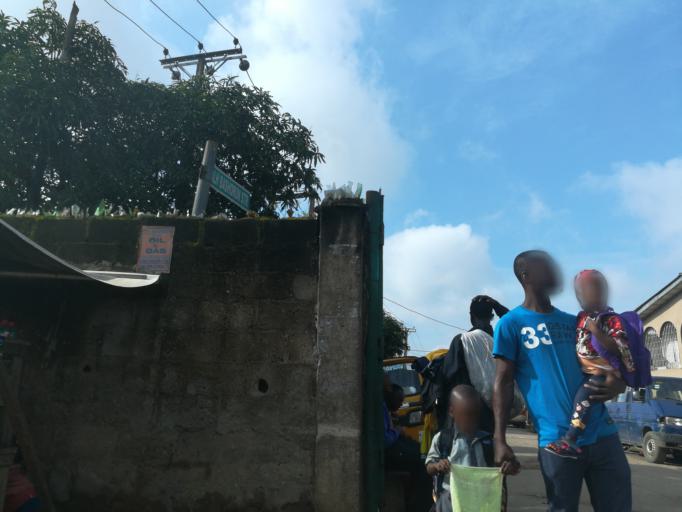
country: NG
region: Lagos
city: Agege
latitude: 6.6177
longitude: 3.3135
